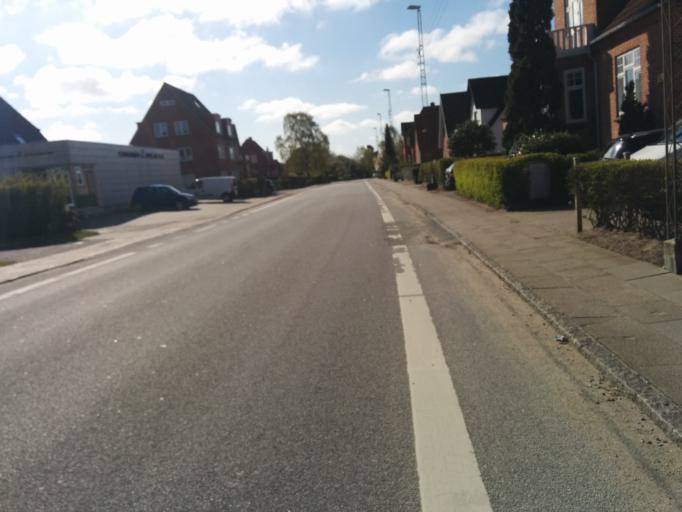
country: DK
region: Central Jutland
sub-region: Viborg Kommune
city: Viborg
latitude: 56.4608
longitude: 9.4062
